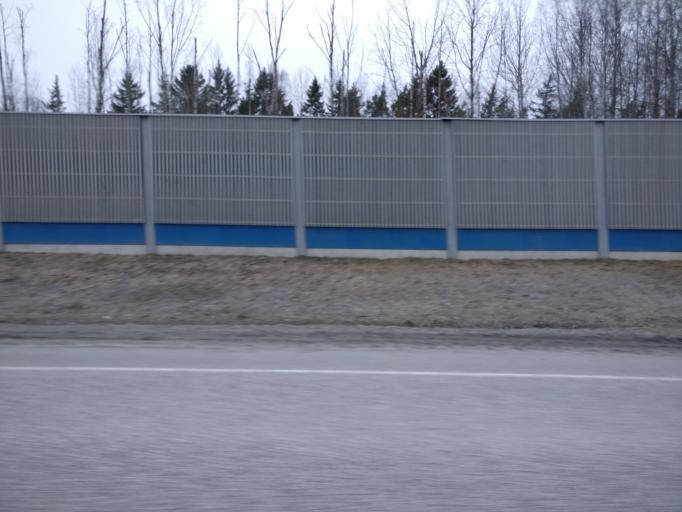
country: FI
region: Uusimaa
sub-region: Helsinki
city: Kilo
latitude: 60.2973
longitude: 24.8530
